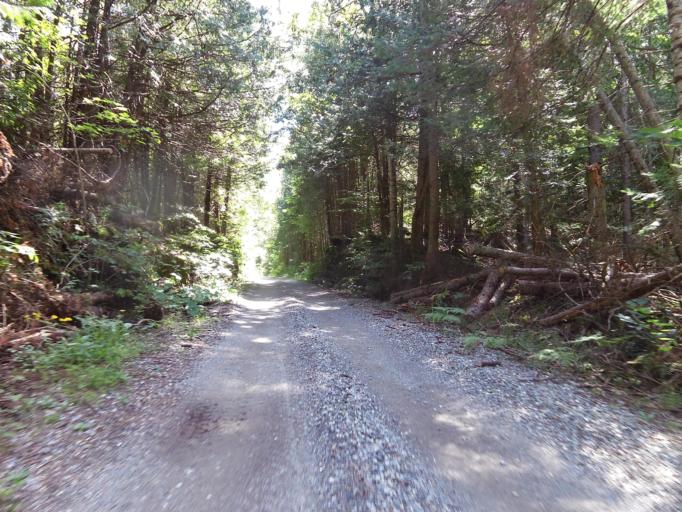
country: CA
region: Ontario
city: Renfrew
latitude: 45.0235
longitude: -76.7046
